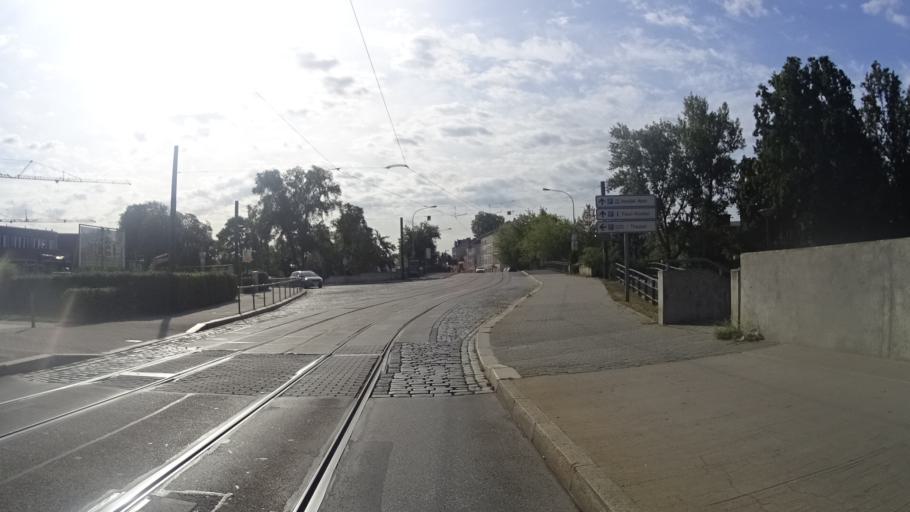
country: DE
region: Brandenburg
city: Brandenburg an der Havel
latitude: 52.4078
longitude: 12.5501
